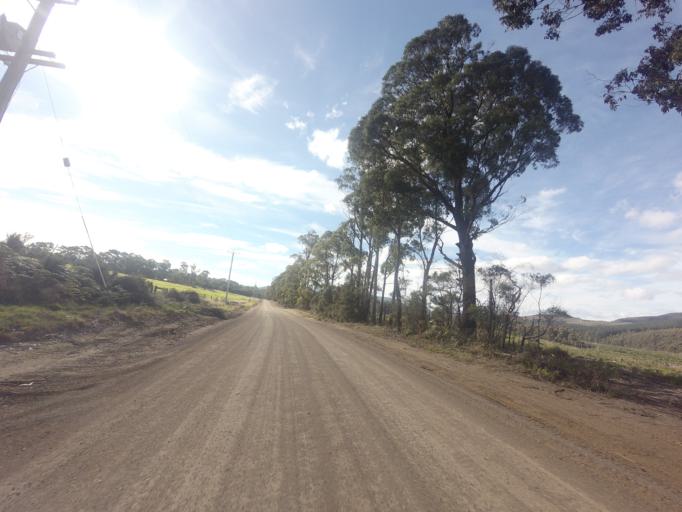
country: AU
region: Tasmania
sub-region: Clarence
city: Sandford
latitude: -43.1673
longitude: 147.7680
